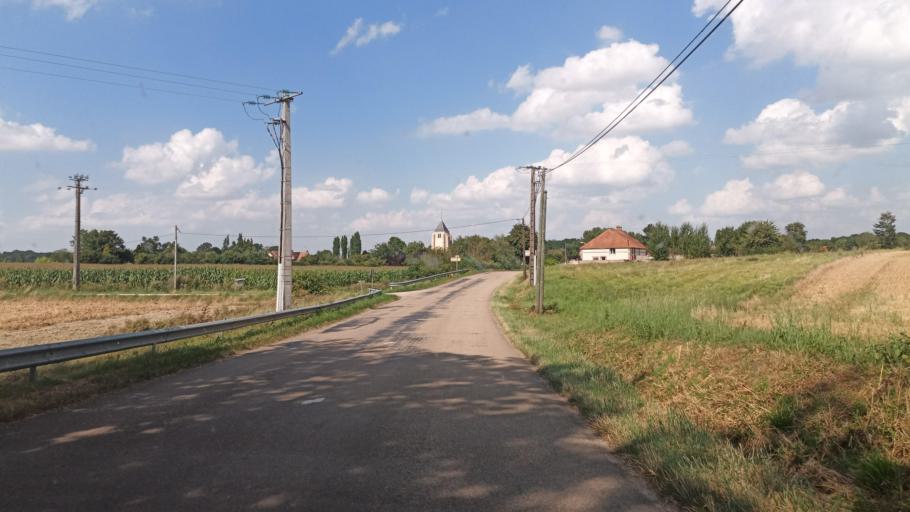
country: FR
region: Centre
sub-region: Departement du Loiret
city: Courtenay
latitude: 48.0133
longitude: 3.1603
